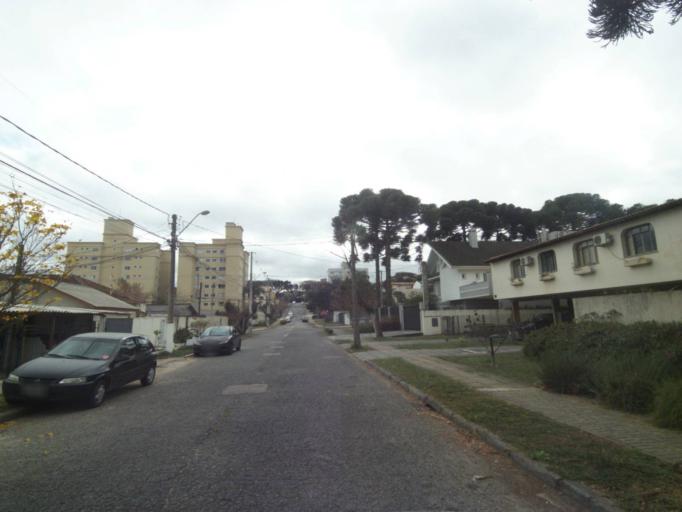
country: BR
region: Parana
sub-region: Curitiba
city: Curitiba
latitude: -25.4577
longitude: -49.2985
